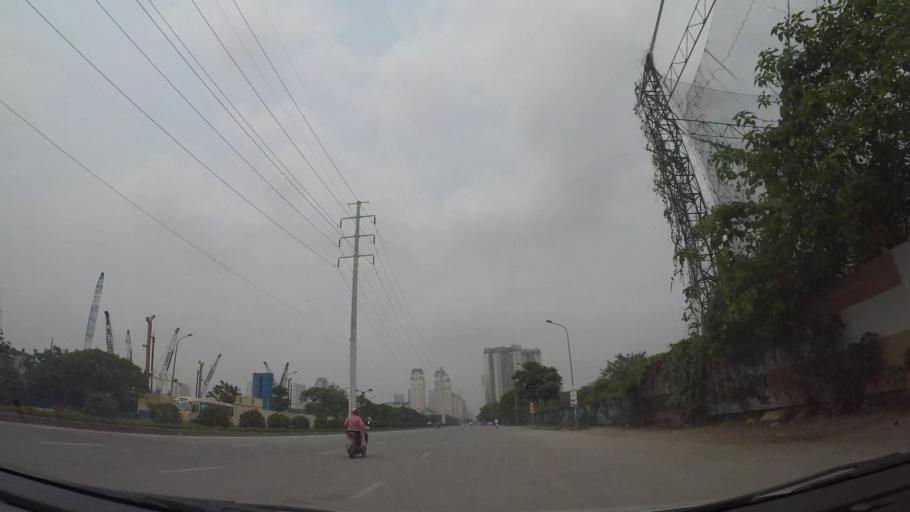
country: VN
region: Ha Noi
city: Cau Dien
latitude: 21.0080
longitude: 105.7690
